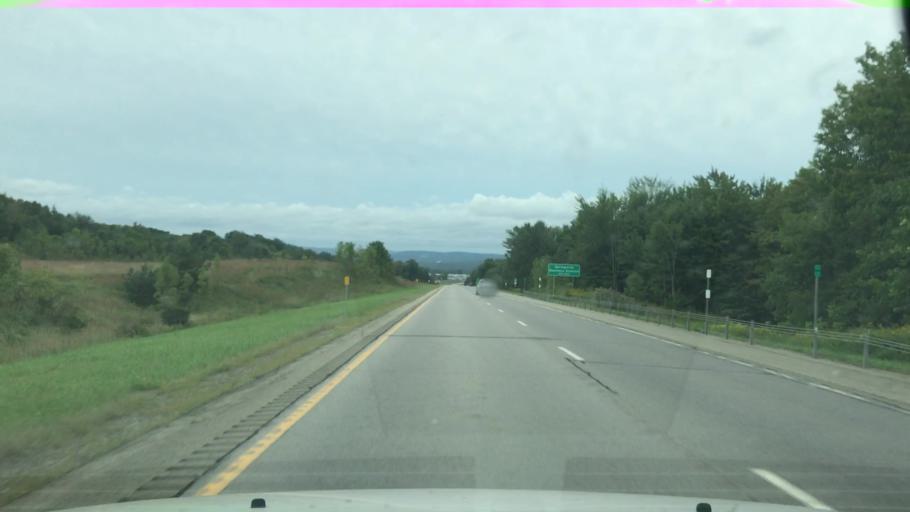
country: US
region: New York
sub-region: Erie County
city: Springville
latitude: 42.5259
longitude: -78.7009
